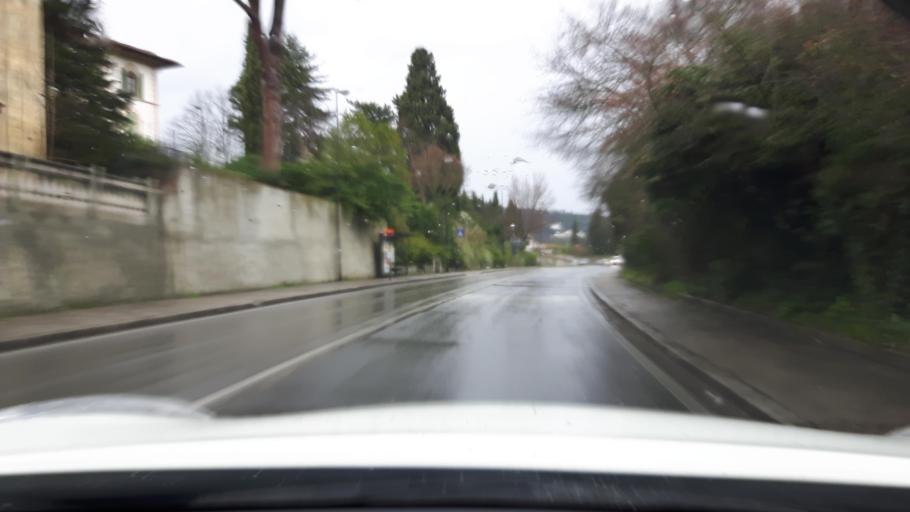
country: IT
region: Tuscany
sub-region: Province of Florence
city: Fiesole
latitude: 43.7982
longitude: 11.2853
